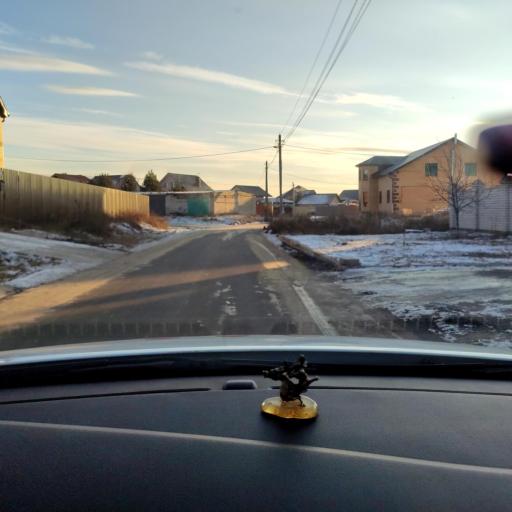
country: RU
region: Tatarstan
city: Stolbishchi
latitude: 55.6092
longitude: 49.1363
